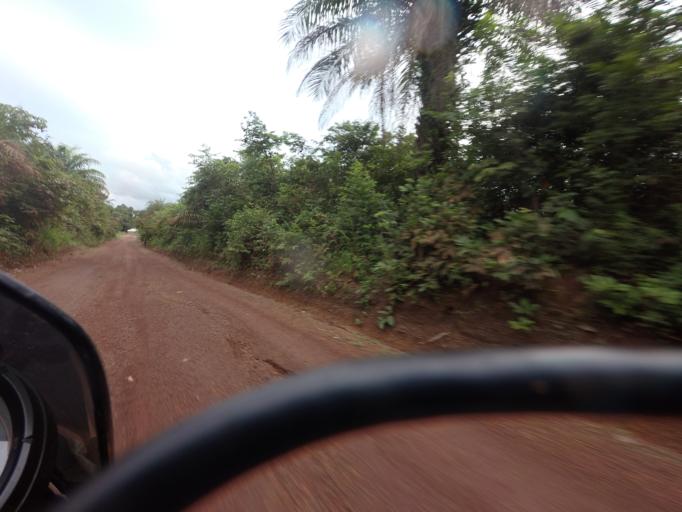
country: SL
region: Northern Province
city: Kambia
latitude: 9.1681
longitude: -12.8777
